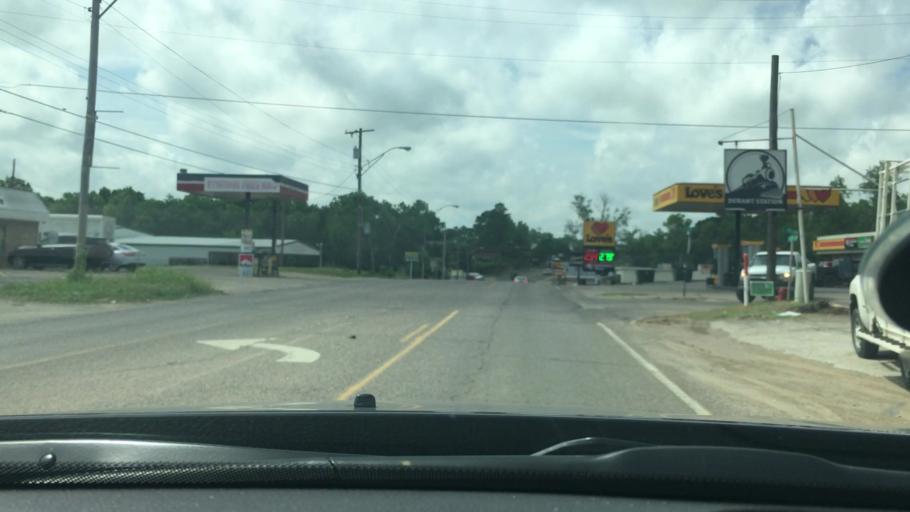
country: US
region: Oklahoma
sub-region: Bryan County
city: Durant
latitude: 34.0029
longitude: -96.3730
